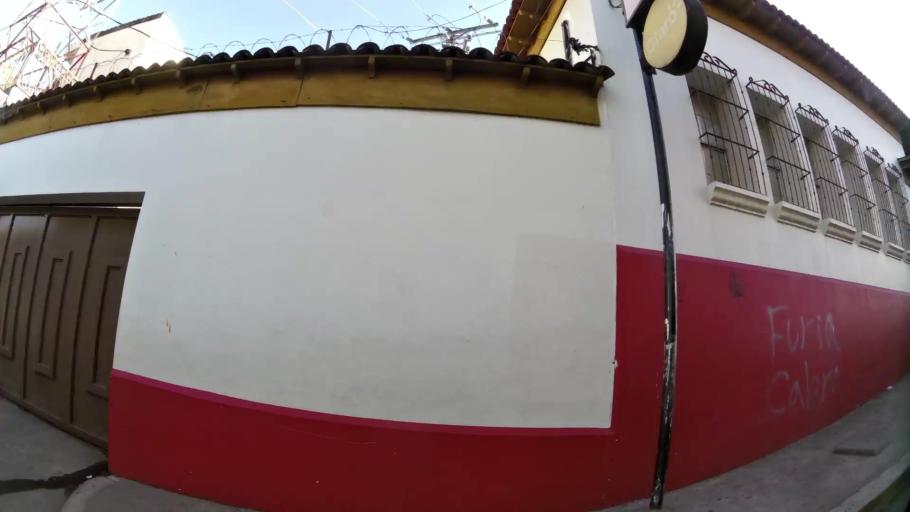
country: SV
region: Santa Ana
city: Metapan
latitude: 14.3305
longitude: -89.4456
